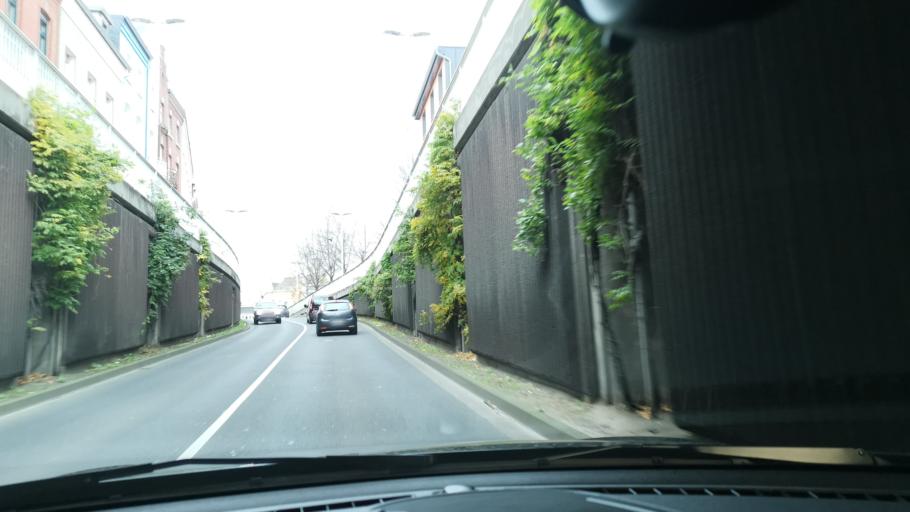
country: DE
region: North Rhine-Westphalia
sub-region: Regierungsbezirk Dusseldorf
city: Grevenbroich
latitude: 51.0839
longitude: 6.5955
